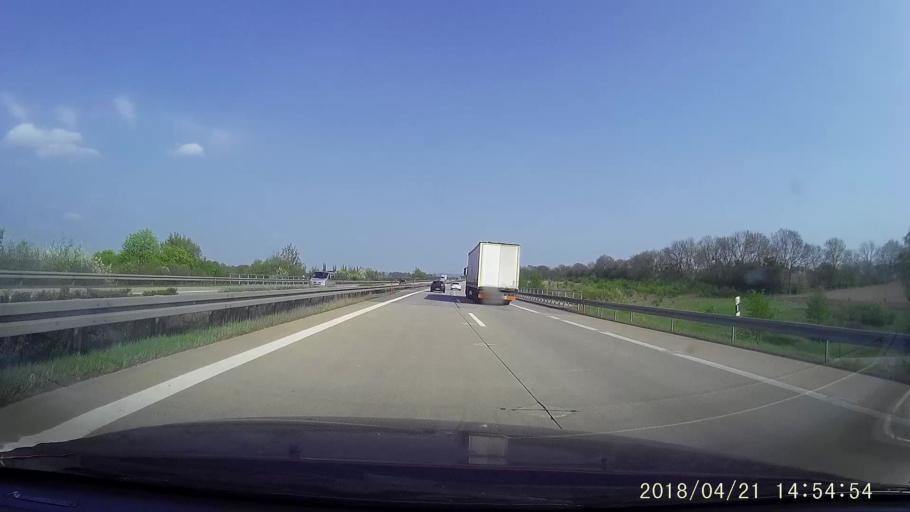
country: DE
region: Saxony
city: Weissenberg
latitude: 51.2109
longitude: 14.6292
